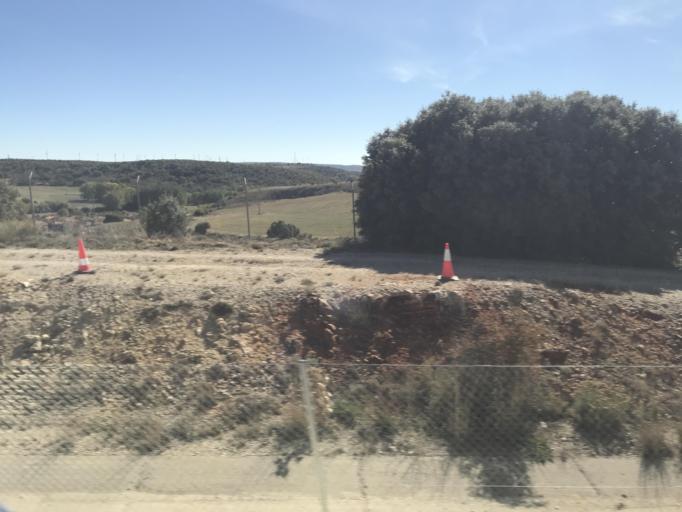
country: ES
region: Castille and Leon
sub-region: Provincia de Soria
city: Medinaceli
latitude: 41.1283
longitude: -2.3385
